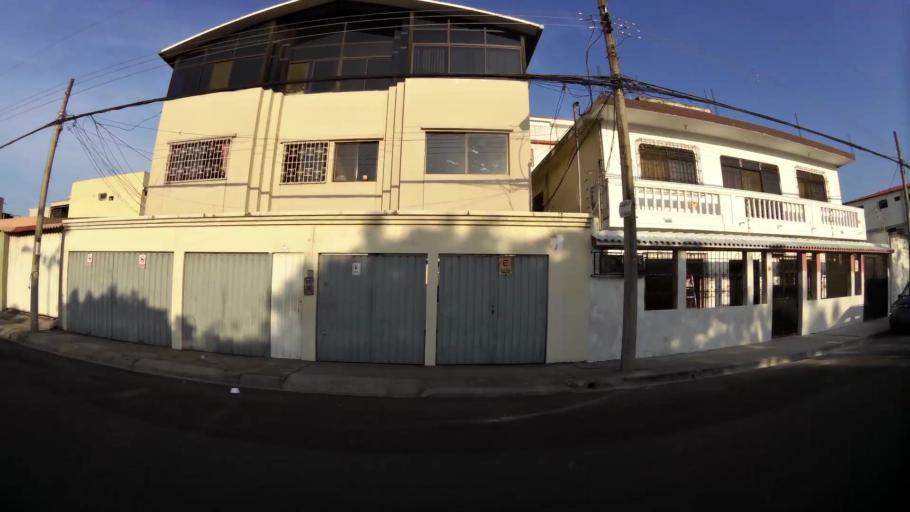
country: EC
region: Guayas
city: Eloy Alfaro
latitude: -2.1585
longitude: -79.8947
